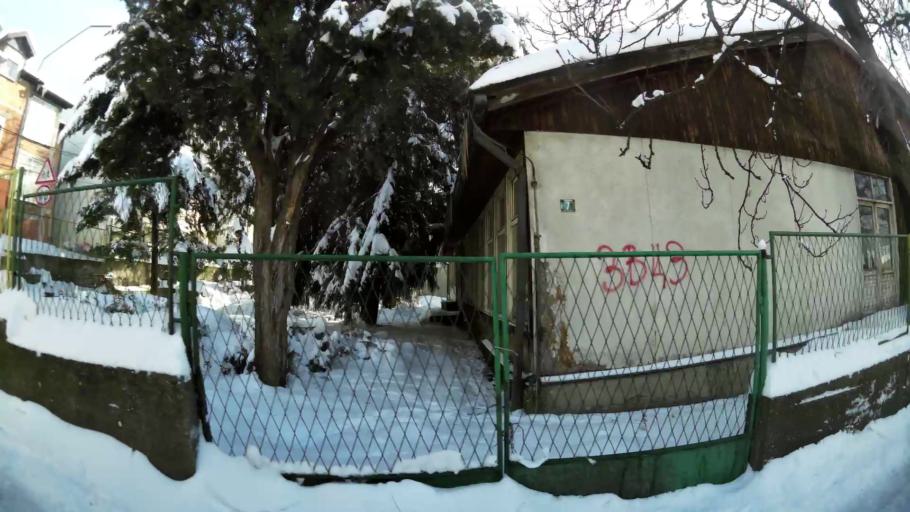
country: RS
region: Central Serbia
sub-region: Belgrade
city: Palilula
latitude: 44.7912
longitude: 20.5077
